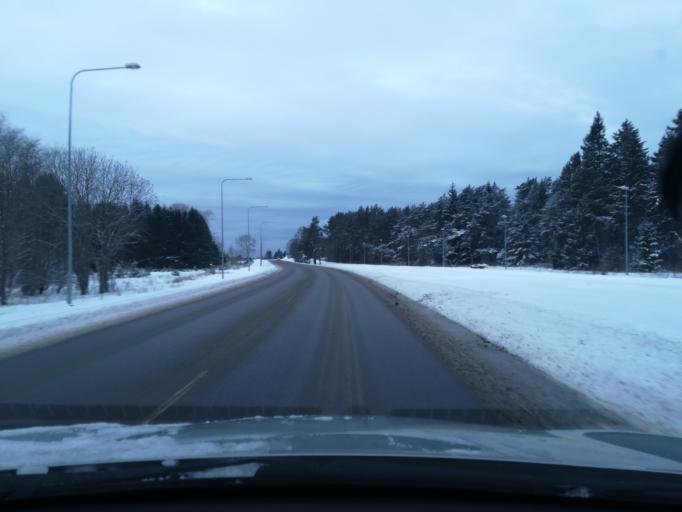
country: EE
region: Harju
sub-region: Harku vald
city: Tabasalu
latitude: 59.4377
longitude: 24.5090
